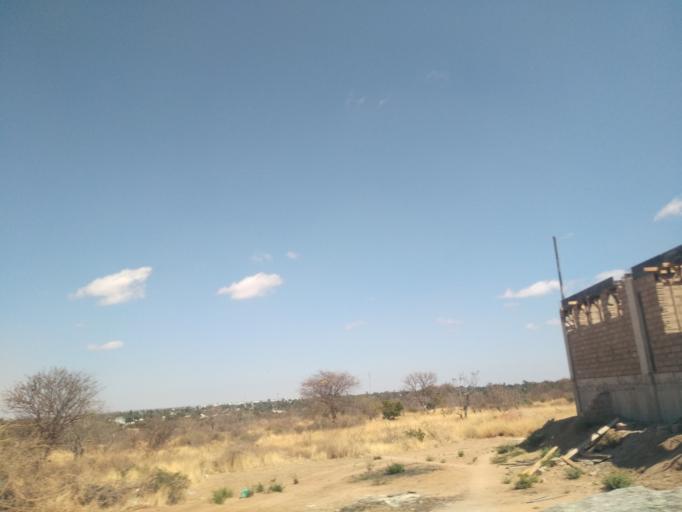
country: TZ
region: Dodoma
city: Dodoma
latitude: -6.1568
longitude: 35.7576
